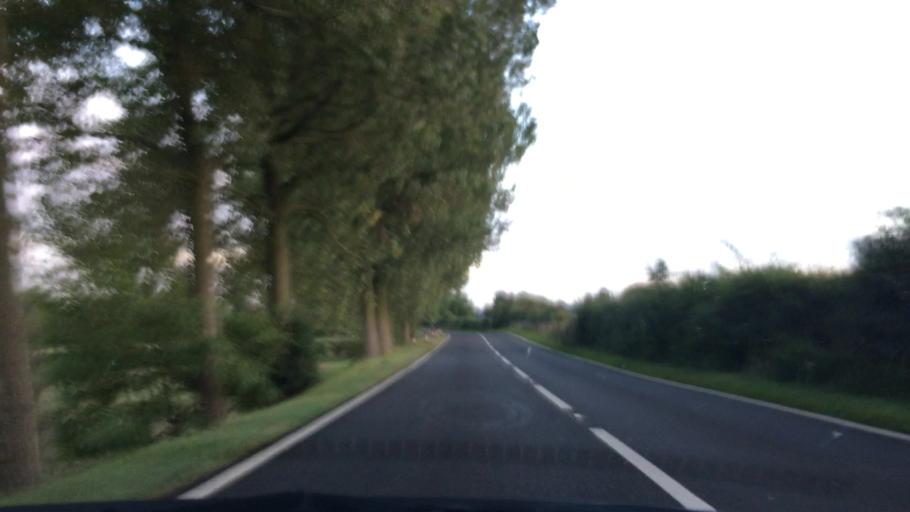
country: GB
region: England
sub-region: North East Lincolnshire
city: Wold Newton
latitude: 53.4678
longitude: -0.1056
